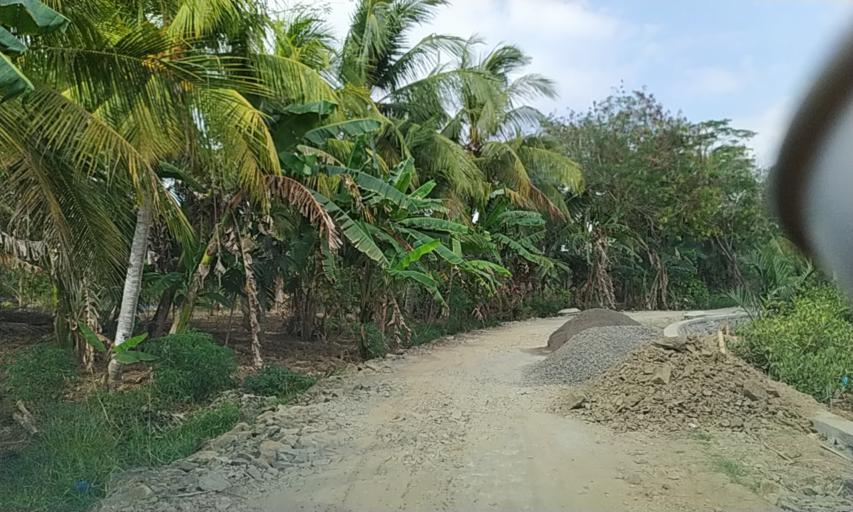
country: ID
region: Central Java
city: Karanganyar
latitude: -7.6462
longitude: 108.8388
